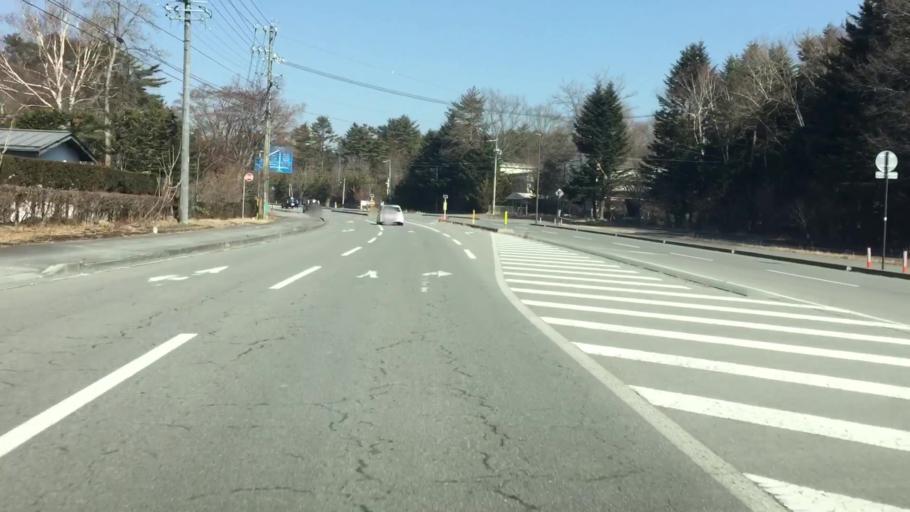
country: JP
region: Nagano
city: Saku
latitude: 36.3190
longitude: 138.6309
